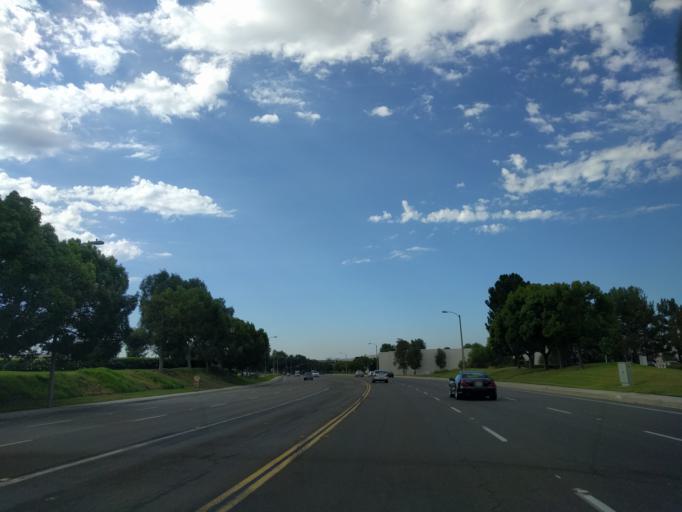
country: US
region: California
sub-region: Orange County
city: Lake Forest
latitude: 33.6607
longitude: -117.7099
